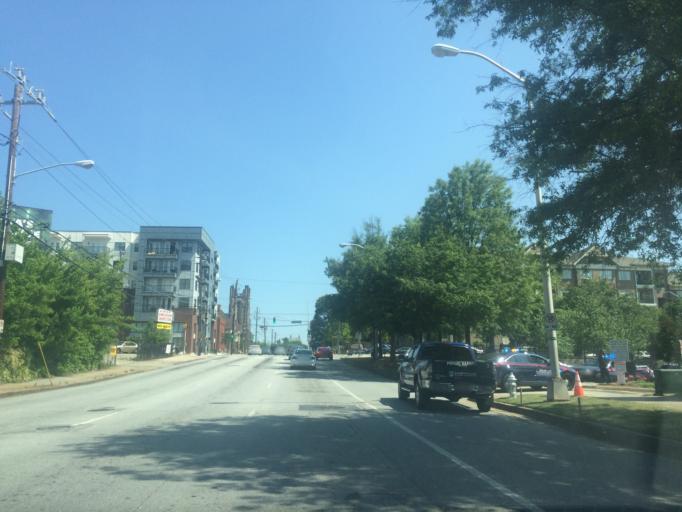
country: US
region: Georgia
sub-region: Fulton County
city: Atlanta
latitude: 33.7705
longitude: -84.3819
